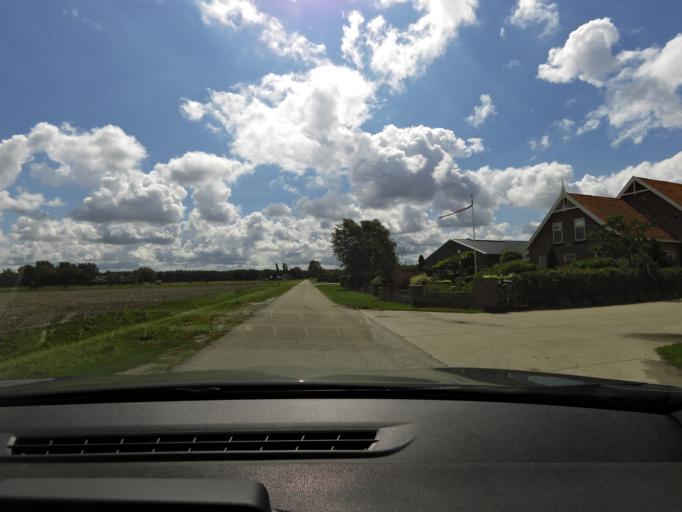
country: NL
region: South Holland
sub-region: Gemeente Hellevoetsluis
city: Nieuw-Helvoet
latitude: 51.8651
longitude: 4.0907
